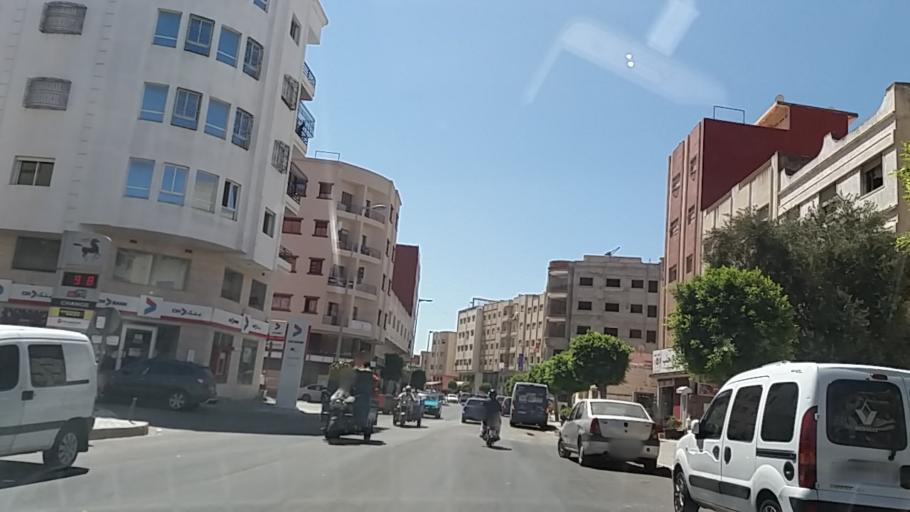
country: MA
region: Tanger-Tetouan
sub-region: Tanger-Assilah
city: Tangier
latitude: 35.7553
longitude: -5.8008
